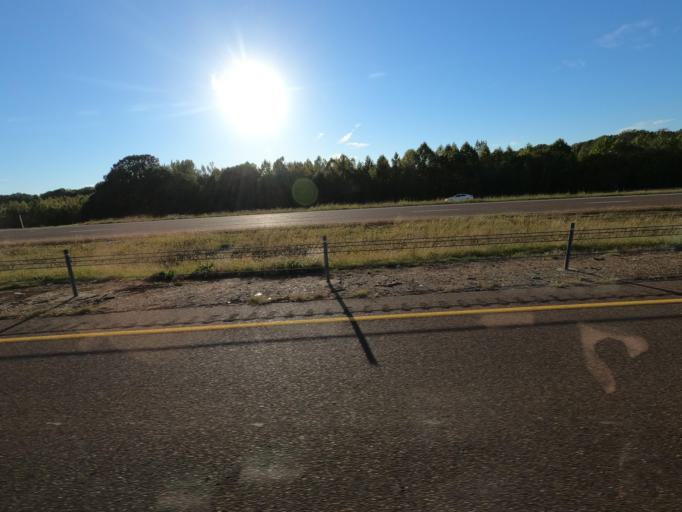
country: US
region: Tennessee
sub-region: Shelby County
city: Arlington
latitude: 35.2593
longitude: -89.6783
